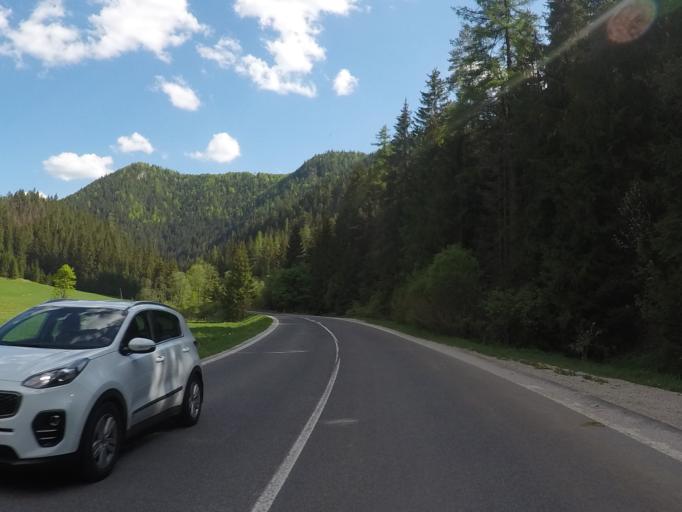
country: SK
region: Kosicky
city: Dobsina
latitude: 48.8815
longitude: 20.3181
